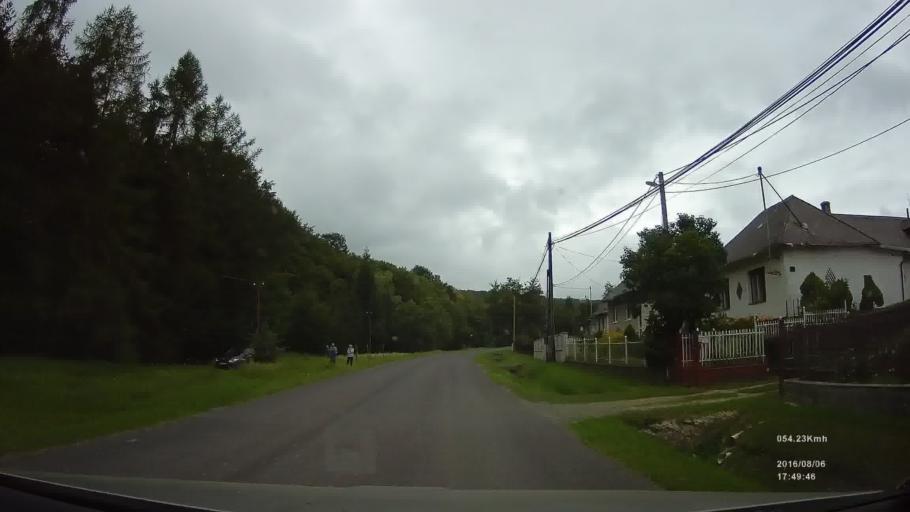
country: SK
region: Presovsky
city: Svidnik
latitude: 49.3859
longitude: 21.5673
